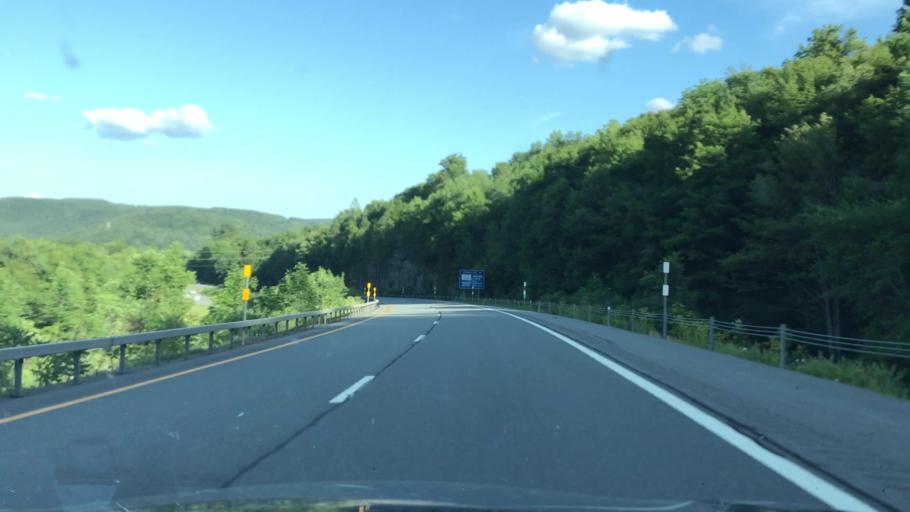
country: US
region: New York
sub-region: Sullivan County
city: Livingston Manor
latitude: 41.9381
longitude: -74.9279
